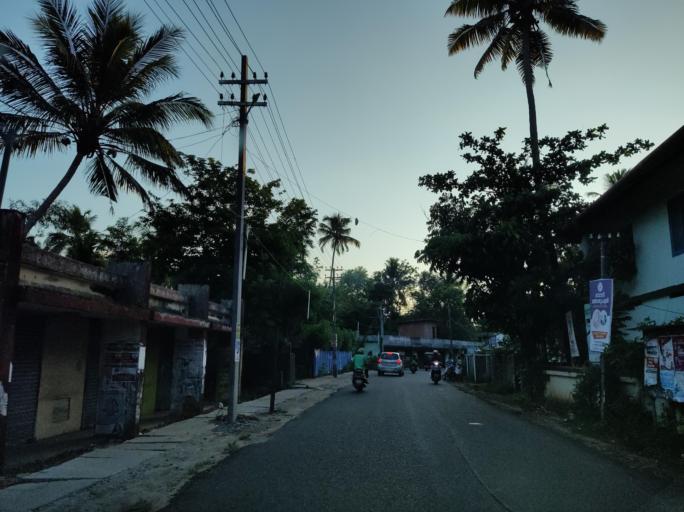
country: IN
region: Kerala
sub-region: Alappuzha
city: Vayalar
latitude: 9.7034
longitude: 76.3142
